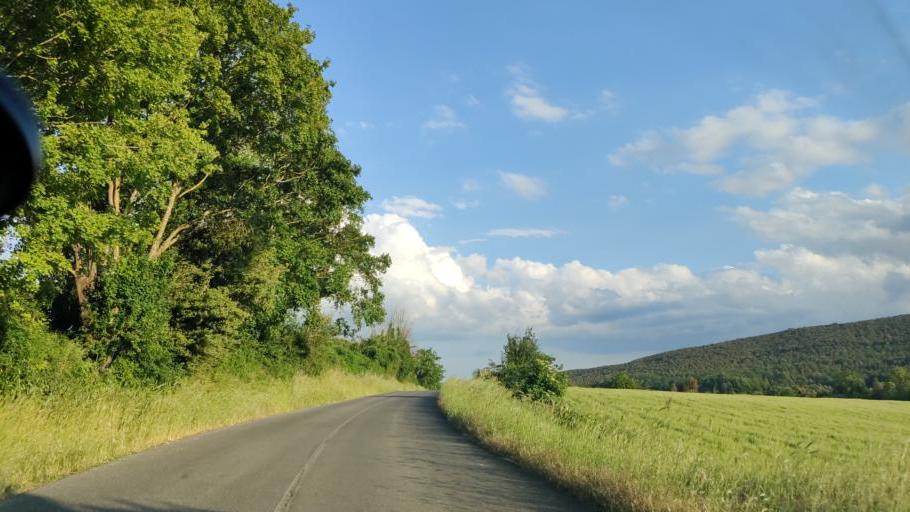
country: IT
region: Umbria
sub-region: Provincia di Terni
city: Lugnano in Teverina
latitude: 42.5847
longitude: 12.3828
